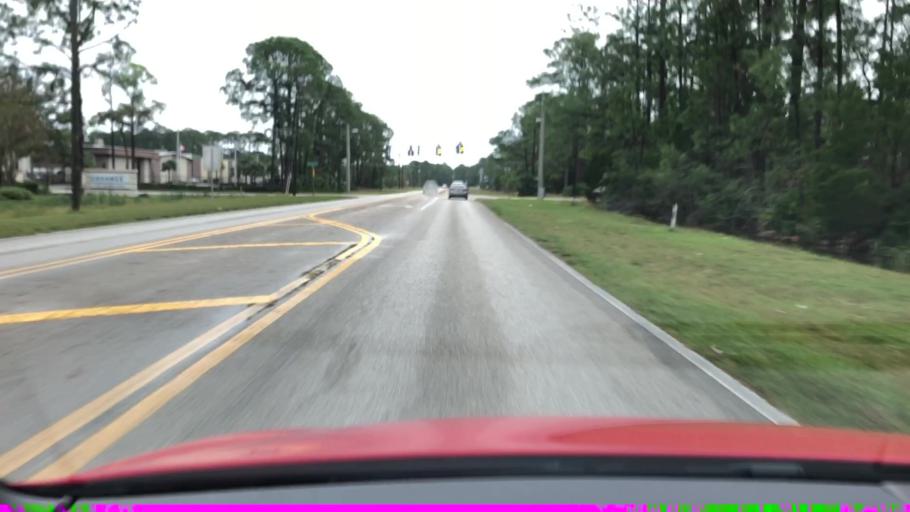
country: US
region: Florida
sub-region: Volusia County
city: Holly Hill
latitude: 29.2122
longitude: -81.0828
